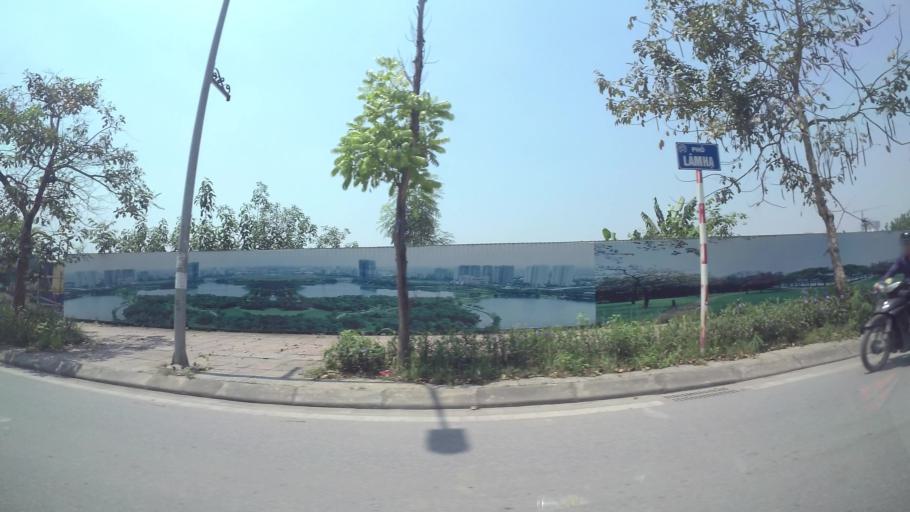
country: VN
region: Ha Noi
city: Hoan Kiem
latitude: 21.0472
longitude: 105.8878
